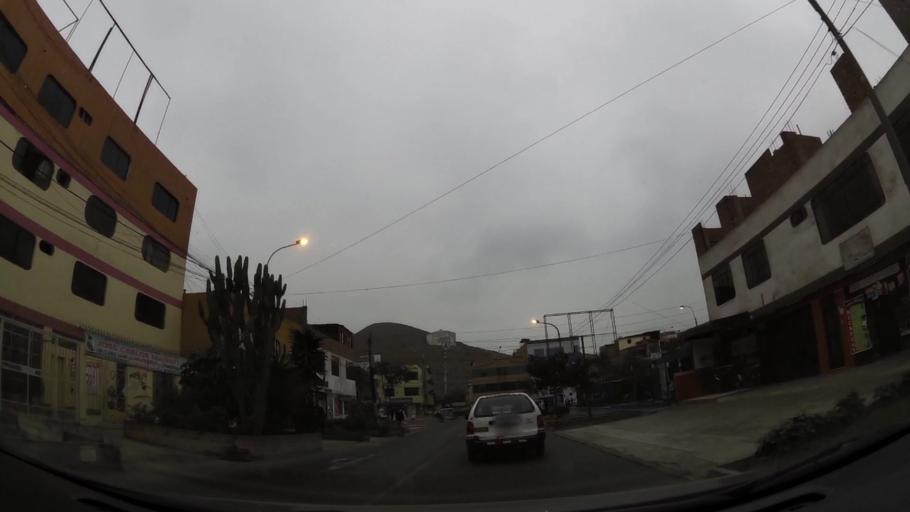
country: PE
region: Lima
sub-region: Lima
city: Independencia
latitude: -11.9375
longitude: -77.0786
